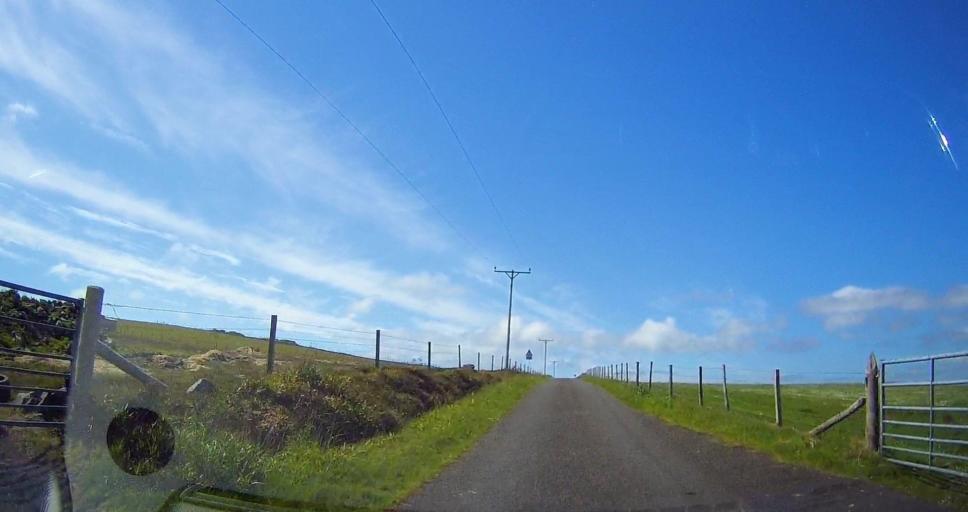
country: GB
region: Scotland
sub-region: Orkney Islands
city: Orkney
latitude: 58.8575
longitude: -2.9414
